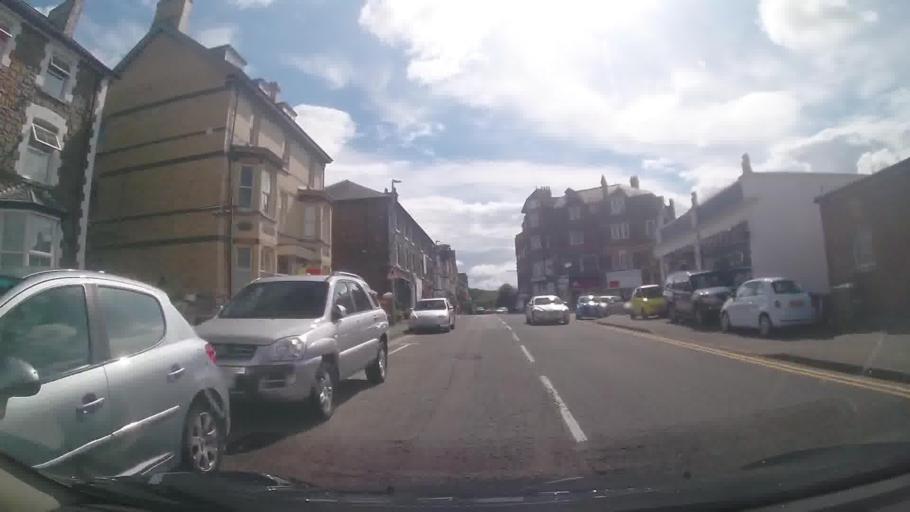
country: GB
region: Wales
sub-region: Sir Powys
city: Llandrindod Wells
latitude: 52.2420
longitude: -3.3774
